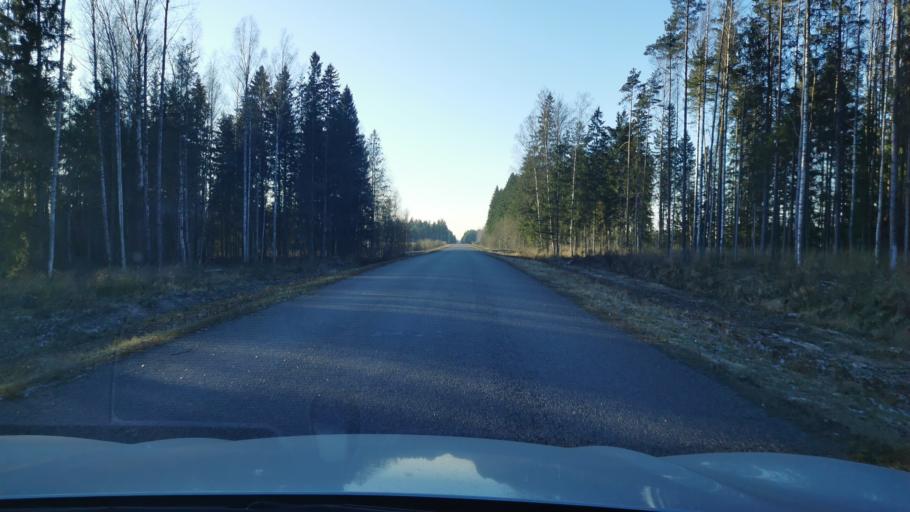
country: EE
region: Ida-Virumaa
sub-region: Kivioli linn
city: Kivioli
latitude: 59.2306
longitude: 26.9686
